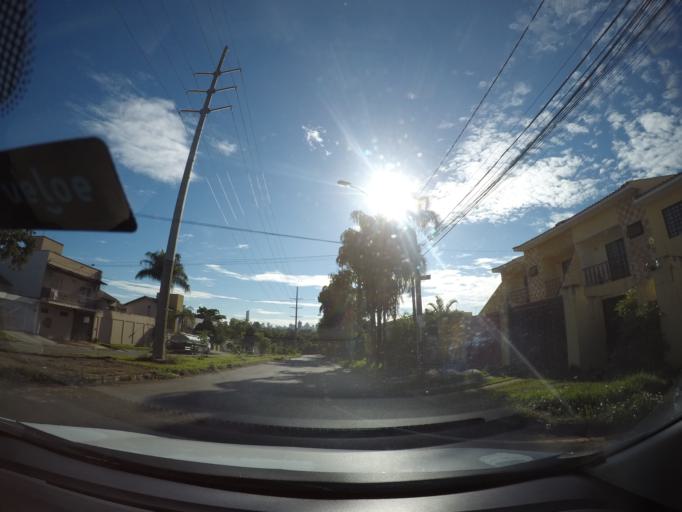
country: BR
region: Goias
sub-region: Goiania
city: Goiania
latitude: -16.7244
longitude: -49.2954
